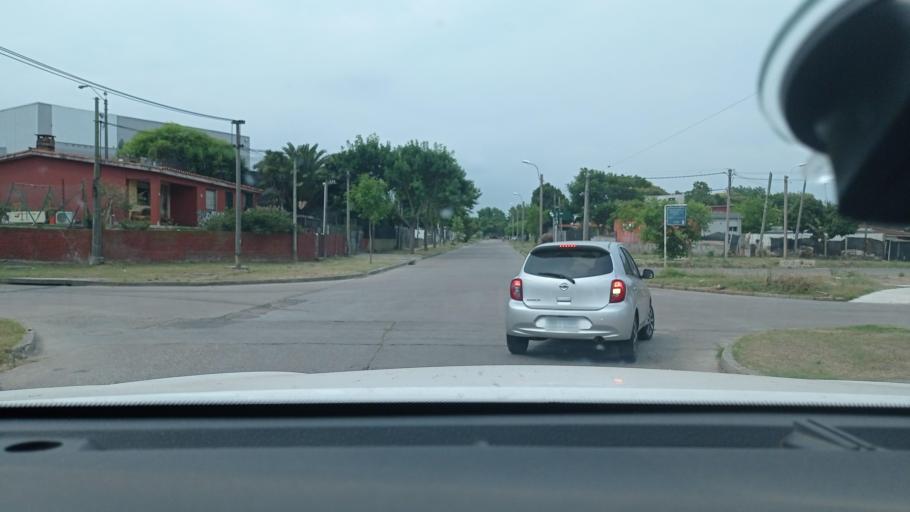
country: UY
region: Canelones
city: Paso de Carrasco
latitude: -34.8731
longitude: -56.0897
